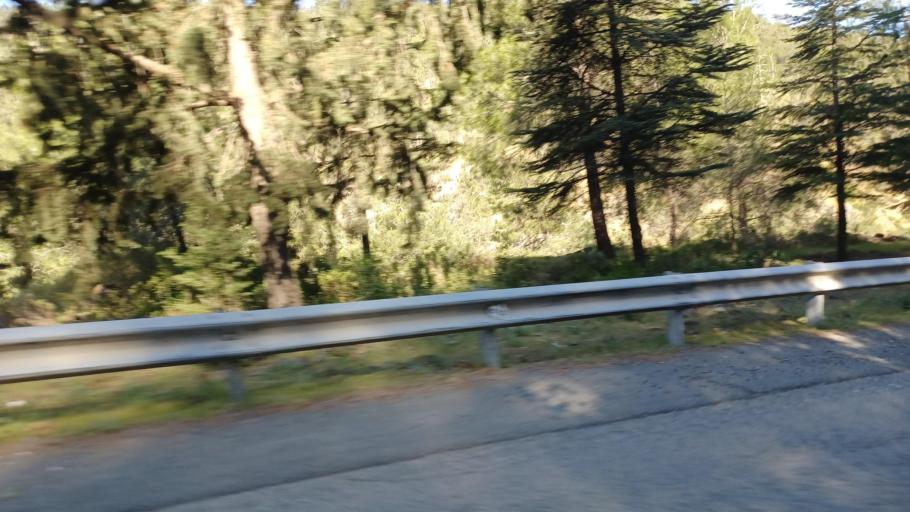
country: CY
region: Limassol
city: Kyperounta
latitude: 35.0131
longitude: 33.0380
